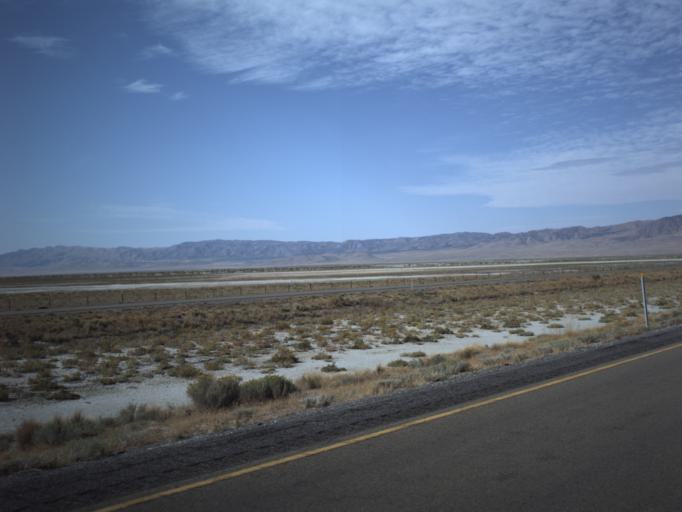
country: US
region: Utah
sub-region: Tooele County
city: Grantsville
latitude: 40.7519
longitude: -112.7105
